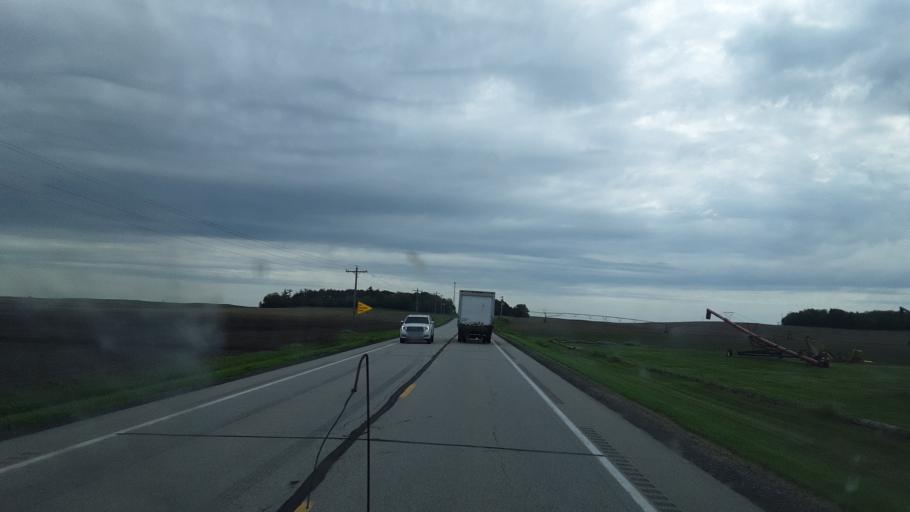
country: US
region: Illinois
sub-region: Mason County
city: Manito
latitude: 40.3034
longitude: -89.7901
